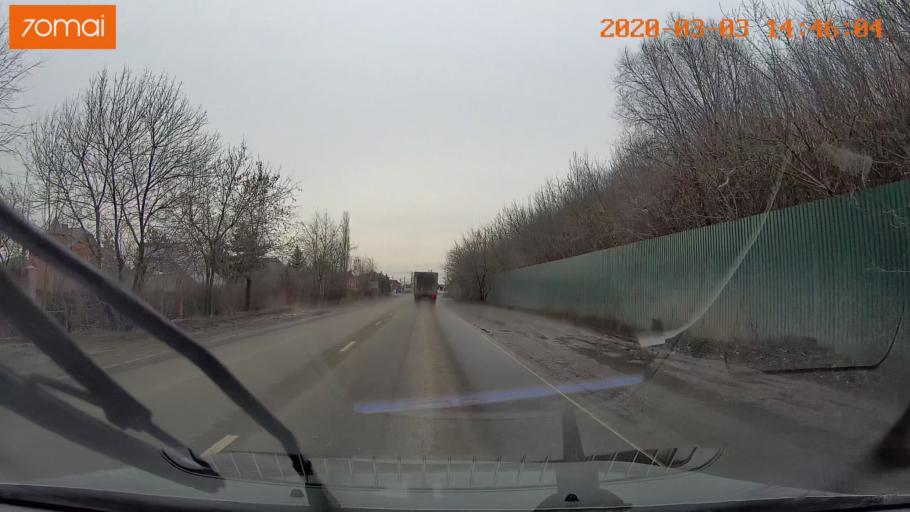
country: RU
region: Moskovskaya
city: Rodniki
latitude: 55.6980
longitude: 38.0556
